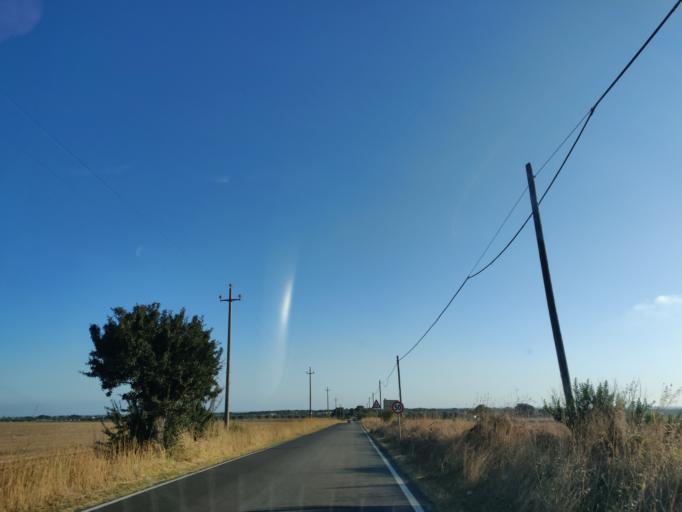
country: IT
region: Latium
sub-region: Provincia di Viterbo
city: Montalto di Castro
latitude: 42.3086
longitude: 11.6532
